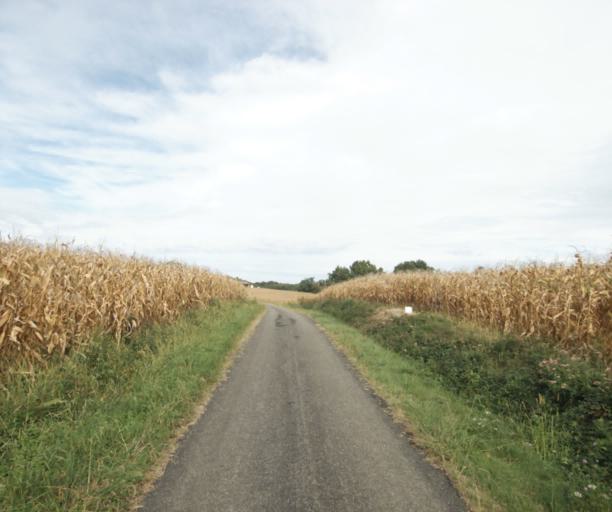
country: FR
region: Midi-Pyrenees
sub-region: Departement du Gers
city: Cazaubon
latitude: 43.9242
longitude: -0.1587
